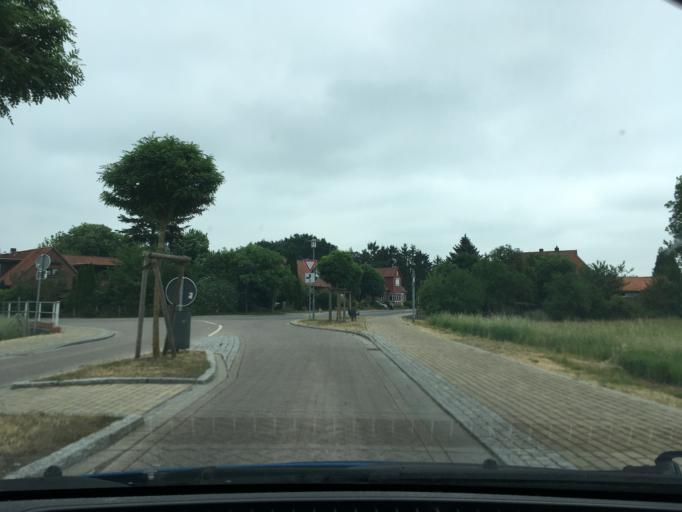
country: DE
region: Lower Saxony
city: Dahlenburg
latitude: 53.1851
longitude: 10.7499
